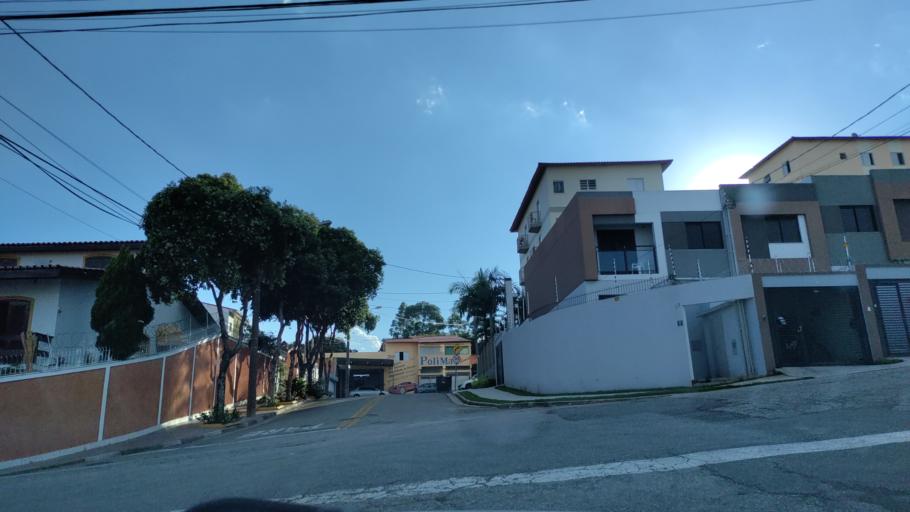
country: BR
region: Sao Paulo
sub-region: Sorocaba
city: Sorocaba
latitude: -23.4811
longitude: -47.4622
